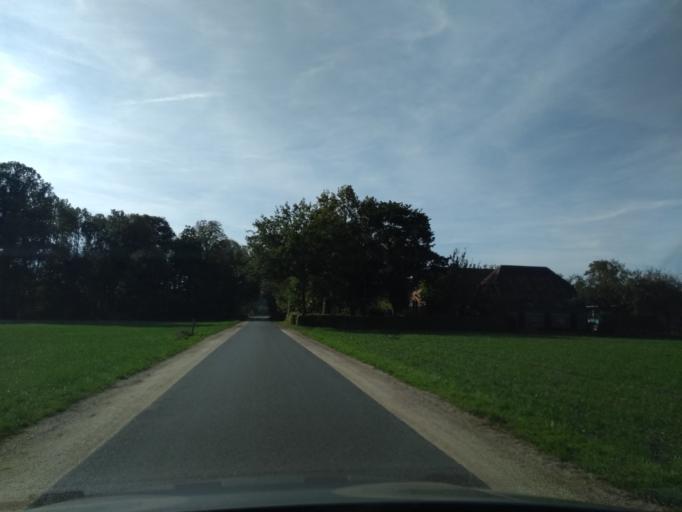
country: NL
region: Gelderland
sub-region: Gemeente Lochem
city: Lochem
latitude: 52.1190
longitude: 6.3792
